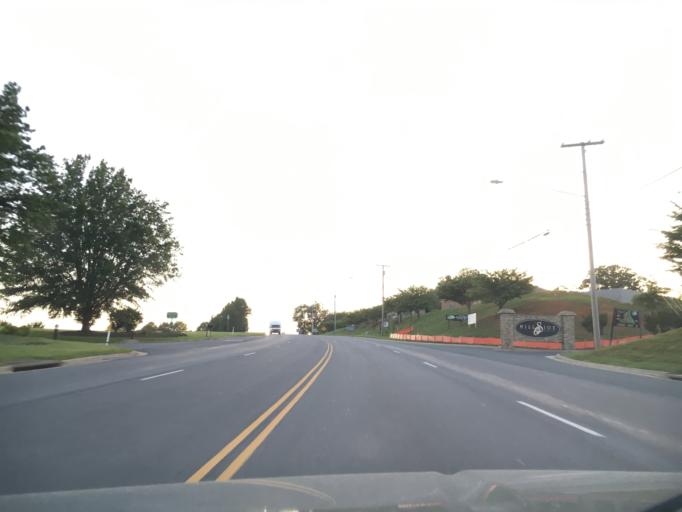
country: US
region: Virginia
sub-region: Bedford County
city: Forest
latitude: 37.3770
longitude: -79.2349
